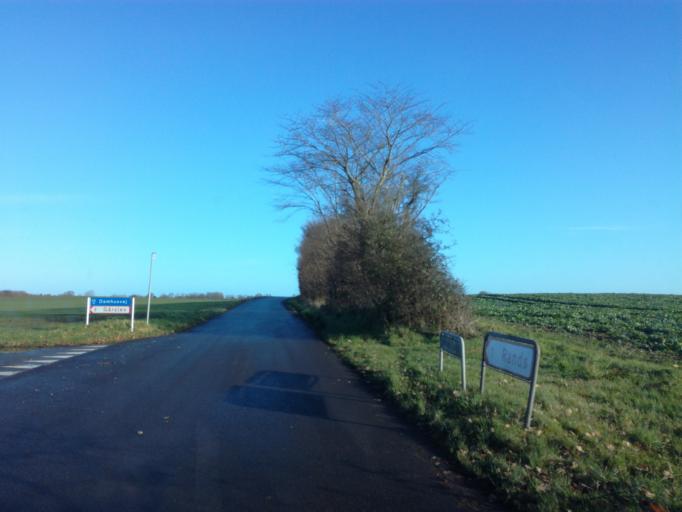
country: DK
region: South Denmark
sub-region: Vejle Kommune
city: Borkop
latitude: 55.6175
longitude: 9.6751
